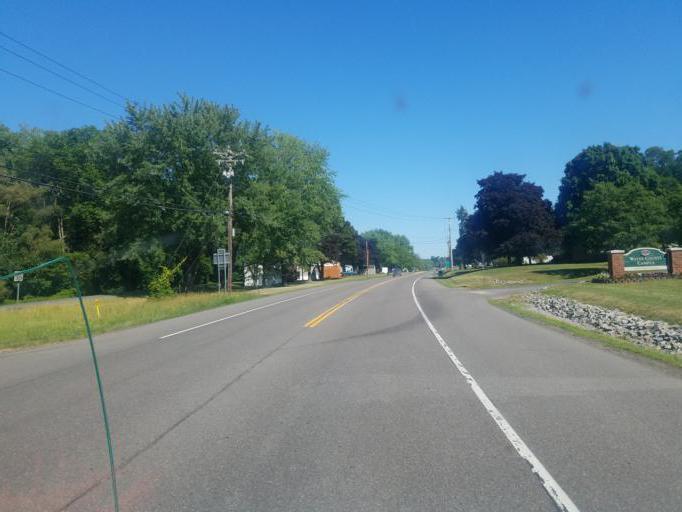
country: US
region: New York
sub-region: Wayne County
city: Lyons
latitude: 43.0673
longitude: -77.0313
